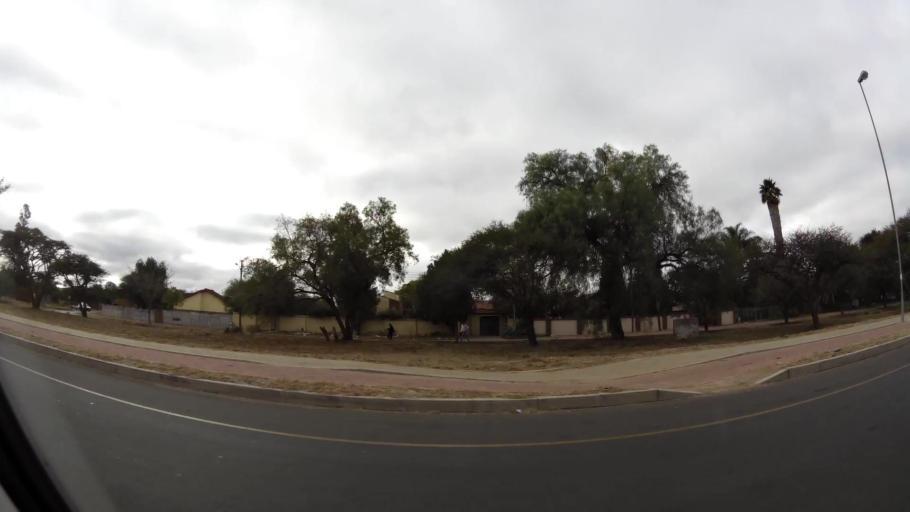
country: ZA
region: Limpopo
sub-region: Capricorn District Municipality
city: Polokwane
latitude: -23.9258
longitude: 29.4516
